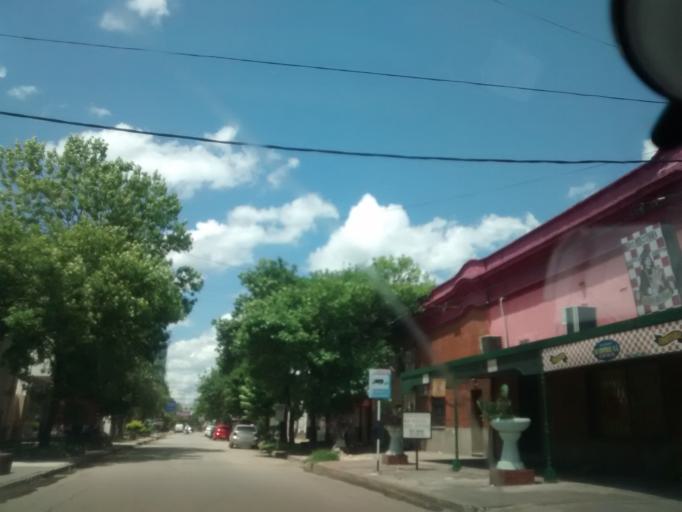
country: AR
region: Chaco
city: Resistencia
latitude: -27.4551
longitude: -58.9891
